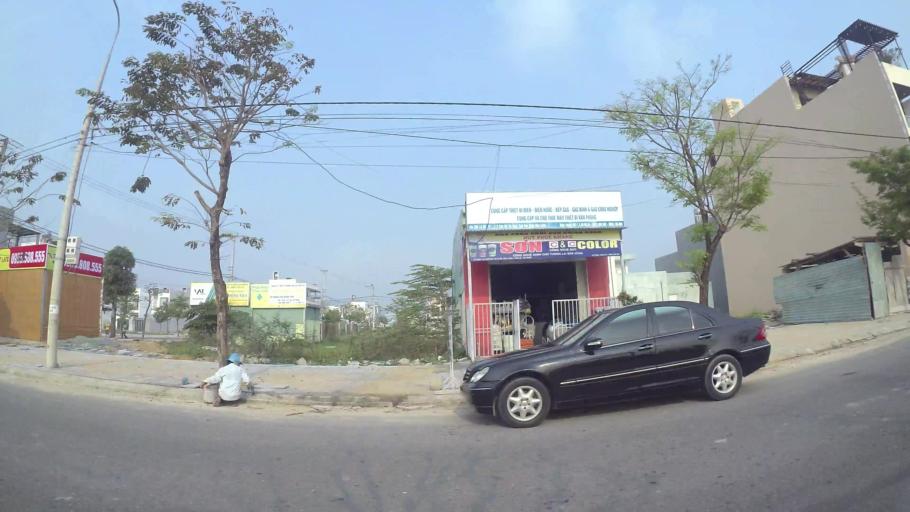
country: VN
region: Da Nang
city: Ngu Hanh Son
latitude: 16.0079
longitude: 108.2288
